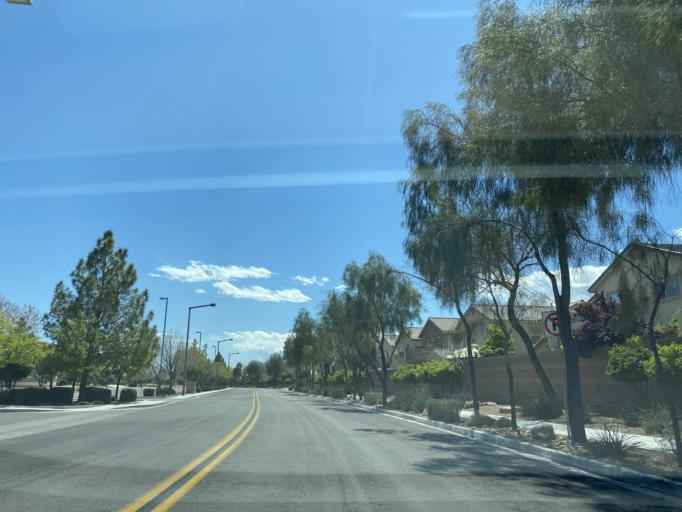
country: US
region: Nevada
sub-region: Clark County
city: North Las Vegas
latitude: 36.3199
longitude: -115.2119
